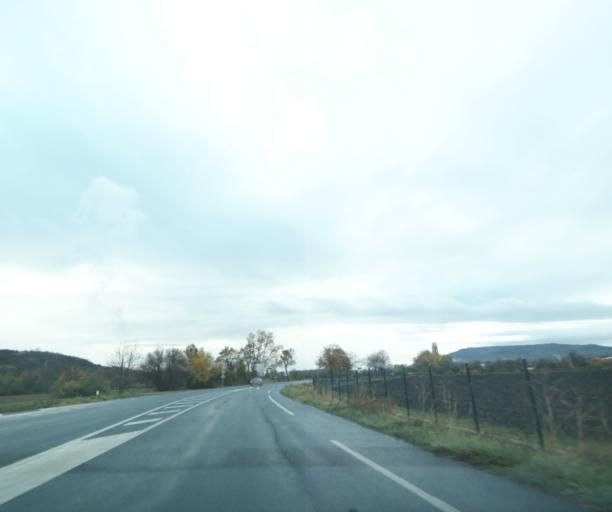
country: FR
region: Auvergne
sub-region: Departement du Puy-de-Dome
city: Aulnat
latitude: 45.7784
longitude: 3.1477
